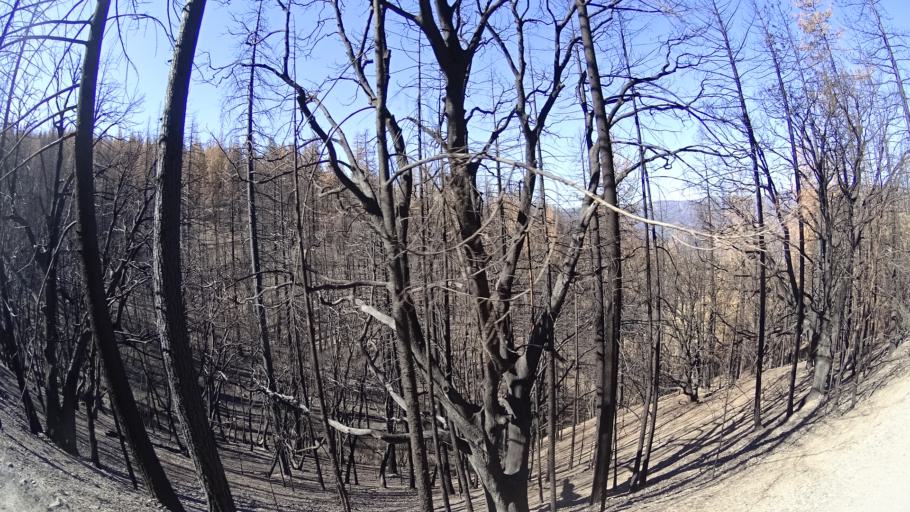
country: US
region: California
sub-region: Tehama County
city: Rancho Tehama Reserve
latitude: 39.6677
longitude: -122.7078
